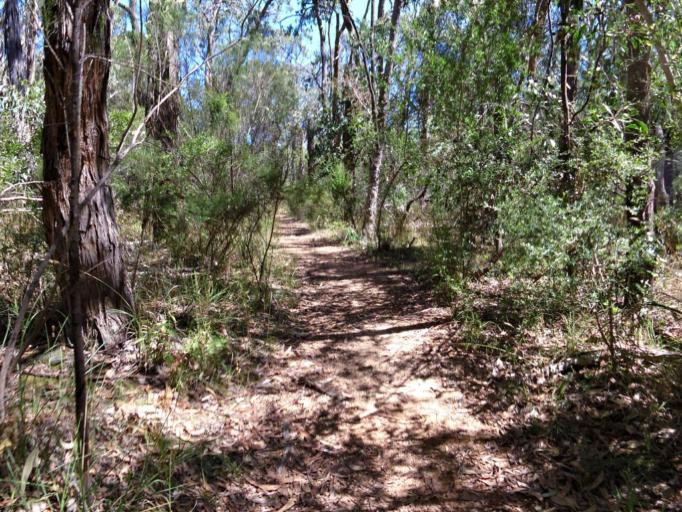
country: AU
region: Victoria
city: Mitcham
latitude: -37.8143
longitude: 145.2075
